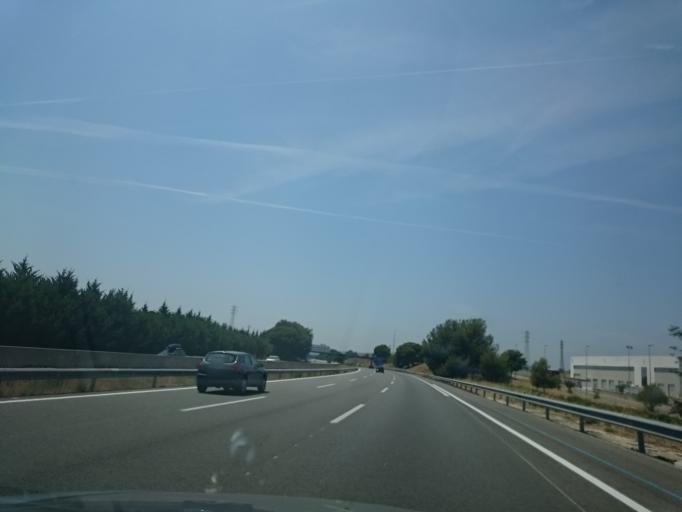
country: ES
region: Catalonia
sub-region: Provincia de Barcelona
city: Vilafranca del Penedes
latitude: 41.3309
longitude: 1.6682
